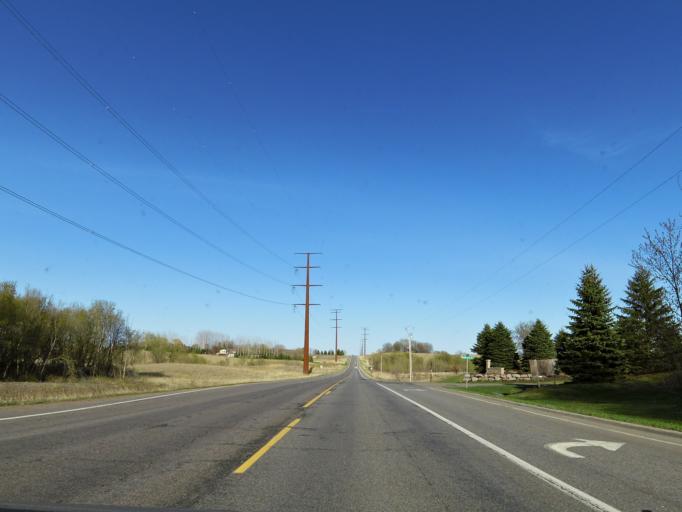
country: US
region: Minnesota
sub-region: Rice County
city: Lonsdale
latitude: 44.5727
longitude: -93.4308
